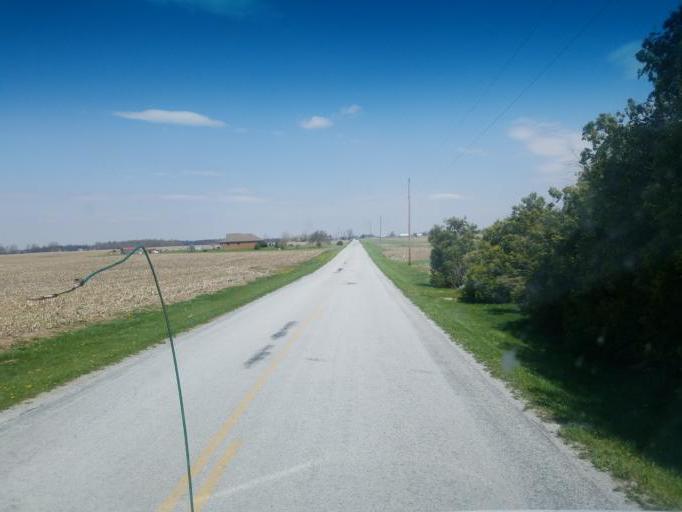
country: US
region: Ohio
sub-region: Hardin County
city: Kenton
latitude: 40.7042
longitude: -83.5379
